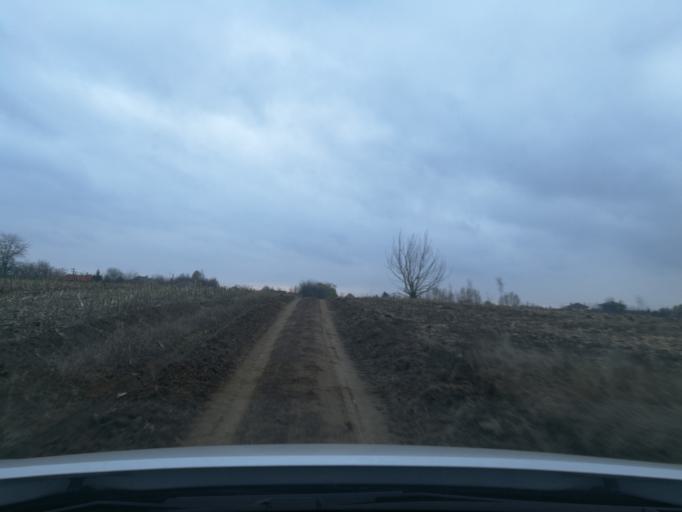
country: HU
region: Szabolcs-Szatmar-Bereg
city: Nyirpazony
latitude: 47.9622
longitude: 21.7844
